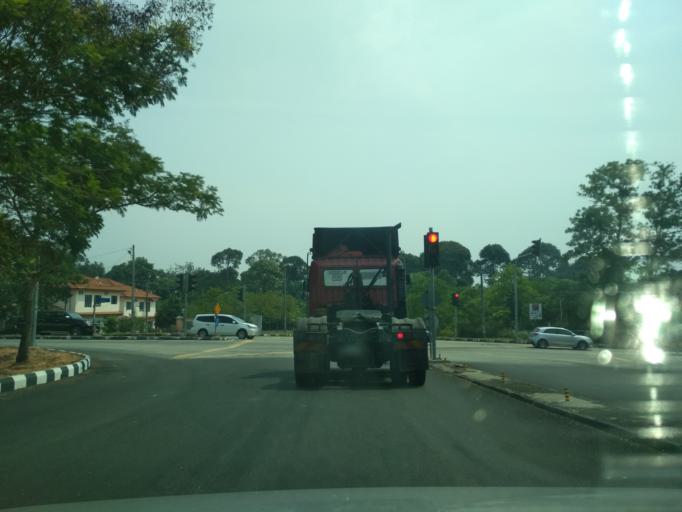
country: MY
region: Kedah
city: Kulim
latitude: 5.3736
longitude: 100.5682
